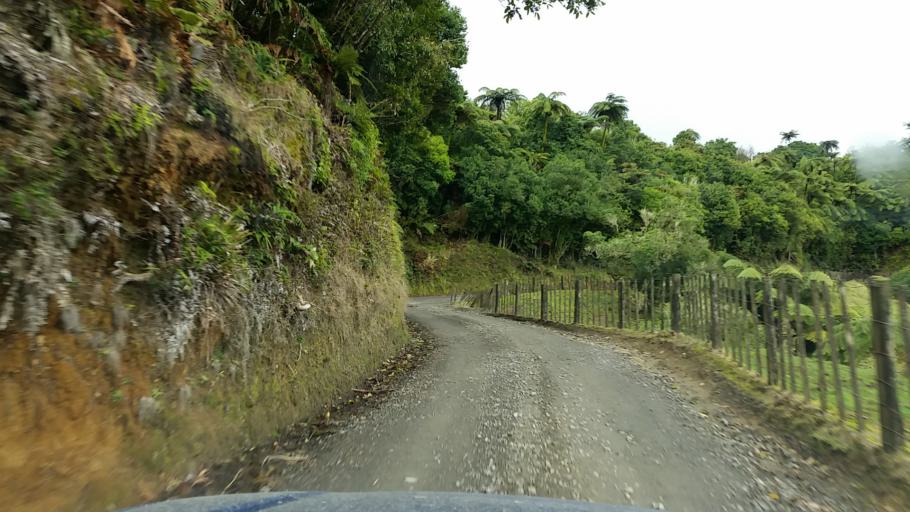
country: NZ
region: Taranaki
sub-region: South Taranaki District
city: Eltham
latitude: -39.1704
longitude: 174.6262
